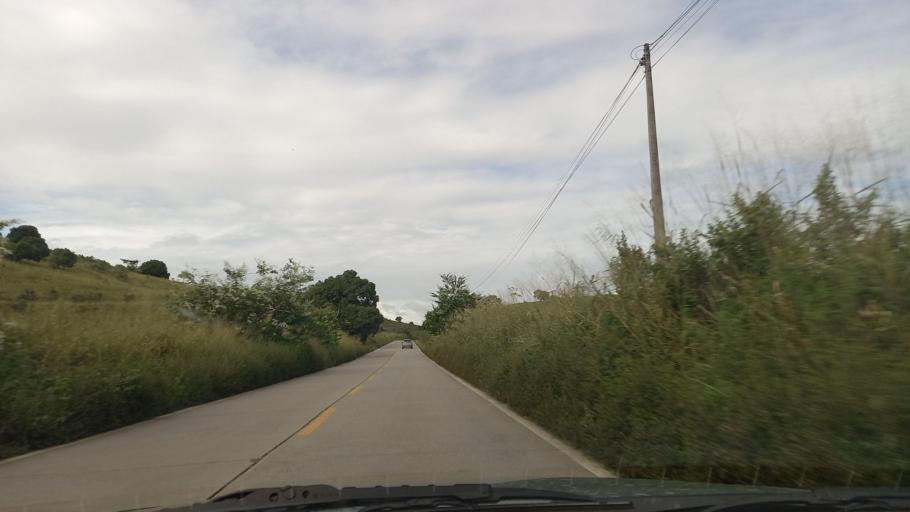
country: BR
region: Pernambuco
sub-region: Catende
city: Catende
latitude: -8.6960
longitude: -35.7322
